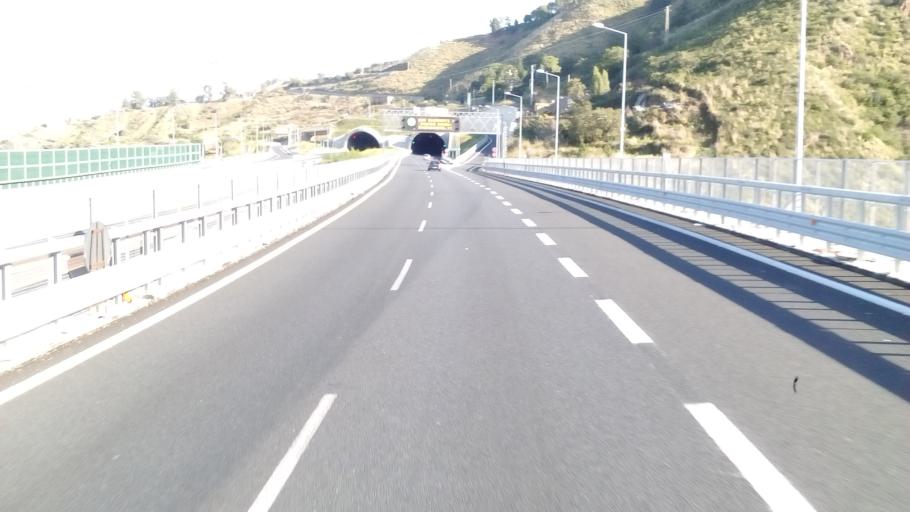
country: IT
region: Calabria
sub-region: Provincia di Reggio Calabria
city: Villa San Giovanni
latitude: 38.2381
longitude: 15.6795
